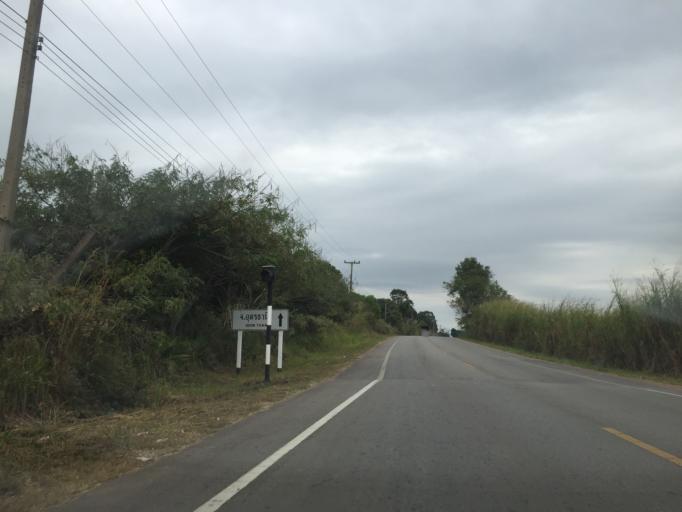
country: TH
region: Loei
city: Phu Ruea
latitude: 17.4465
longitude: 101.4940
